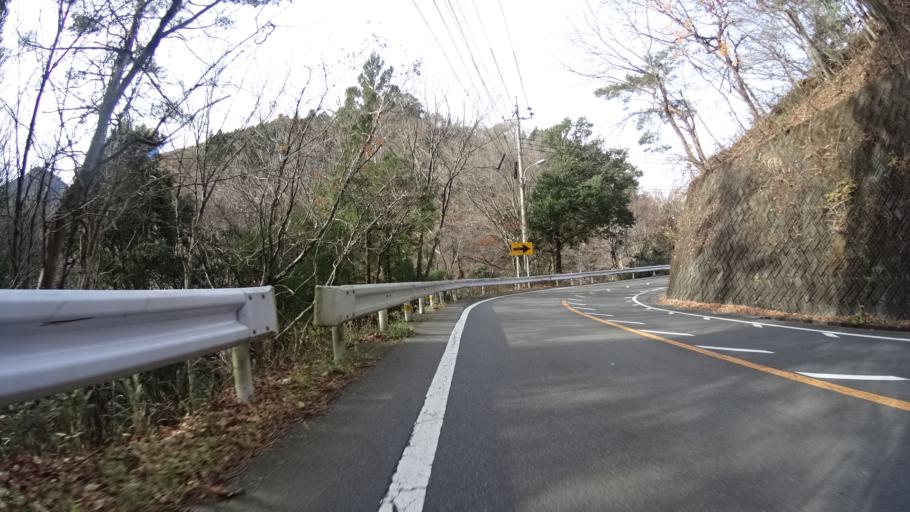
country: JP
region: Yamanashi
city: Uenohara
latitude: 35.5320
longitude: 139.0952
